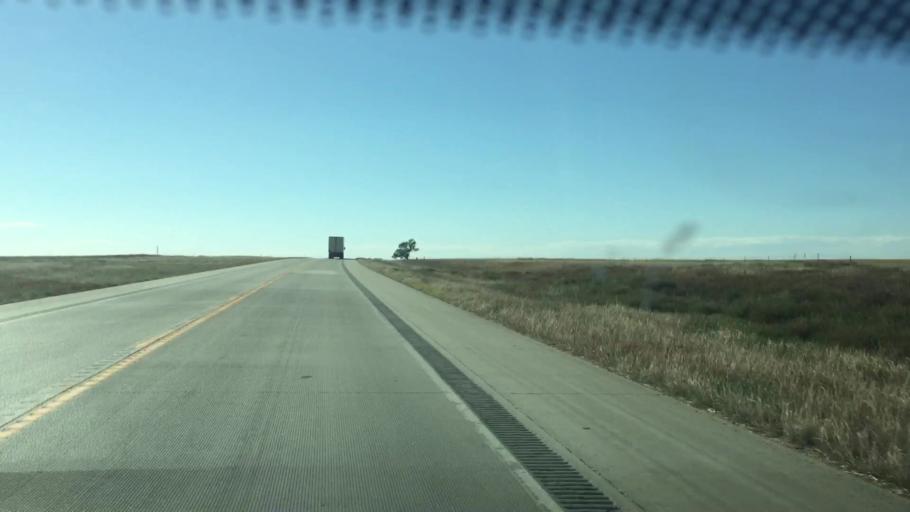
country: US
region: Colorado
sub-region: Kiowa County
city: Eads
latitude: 38.7639
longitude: -102.8224
